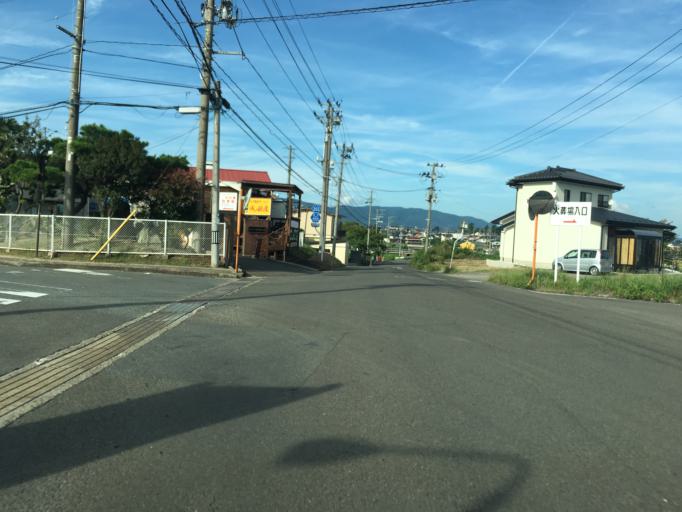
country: JP
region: Fukushima
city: Hobaramachi
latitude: 37.8351
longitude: 140.5084
